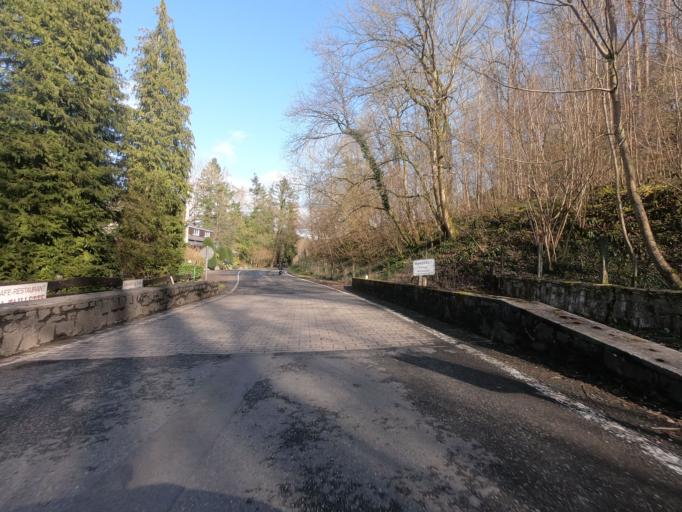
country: BE
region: Wallonia
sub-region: Province de Namur
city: Mettet
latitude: 50.3006
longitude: 4.7408
